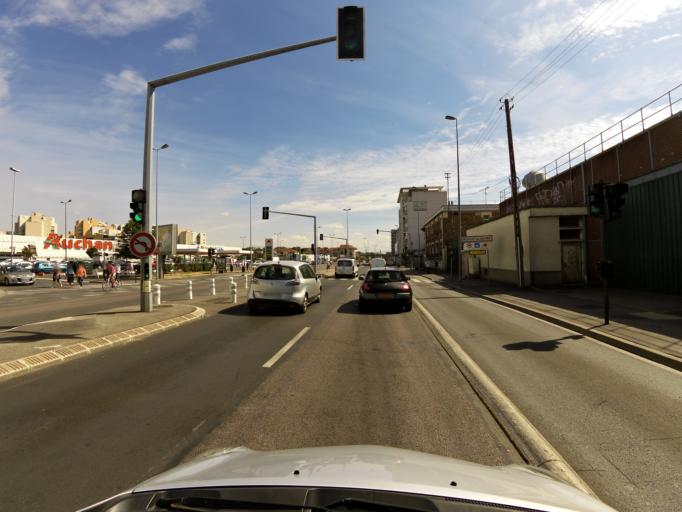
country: FR
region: Ile-de-France
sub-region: Departement de Seine-Saint-Denis
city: Neuilly-Plaisance
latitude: 48.8534
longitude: 2.5162
